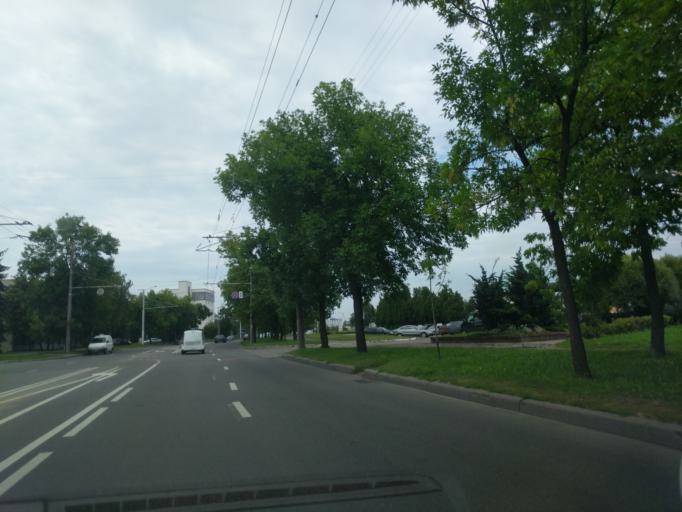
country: BY
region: Minsk
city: Novoye Medvezhino
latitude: 53.8829
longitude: 27.4826
